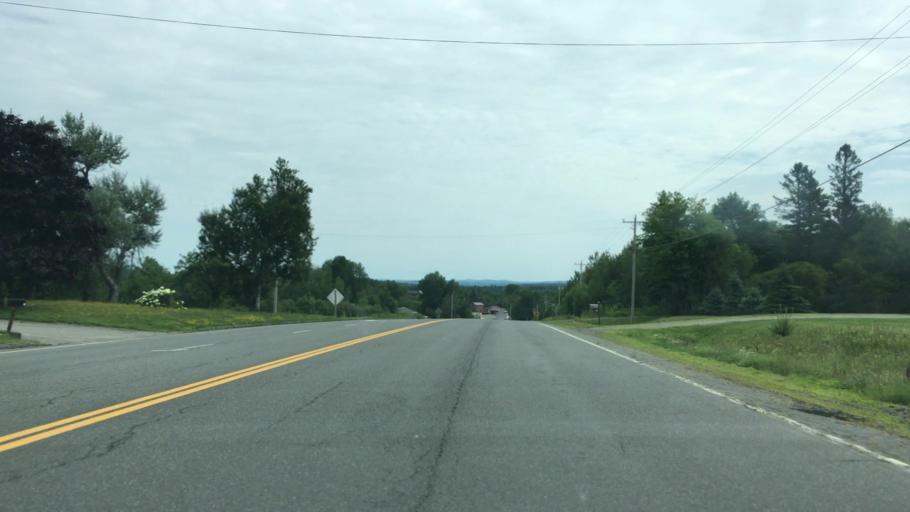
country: US
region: Maine
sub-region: Washington County
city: Calais
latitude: 45.0926
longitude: -67.4755
